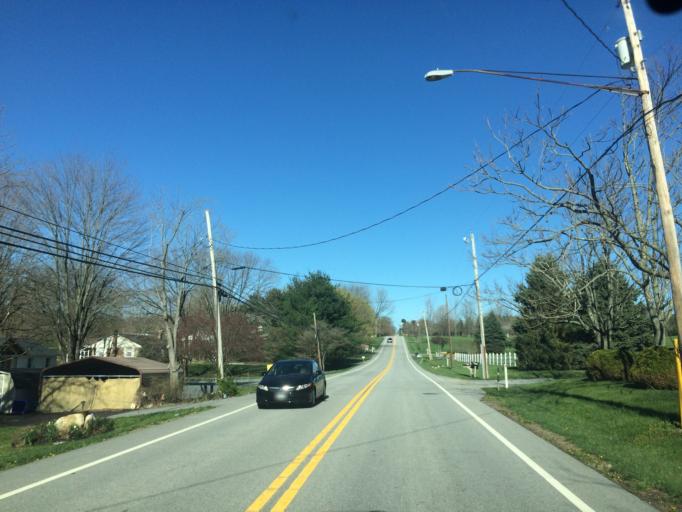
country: US
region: Maryland
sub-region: Carroll County
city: Mount Airy
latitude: 39.3386
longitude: -77.0791
